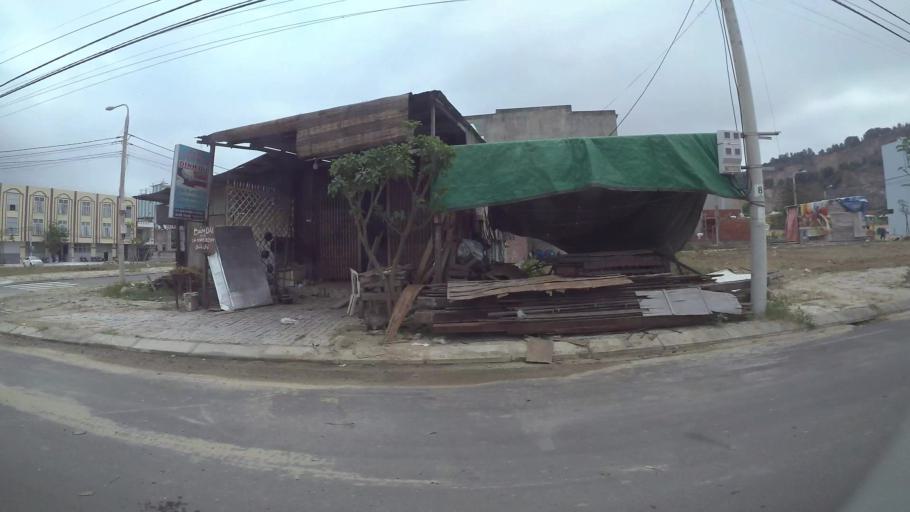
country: VN
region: Da Nang
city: Lien Chieu
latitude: 16.0452
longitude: 108.1646
